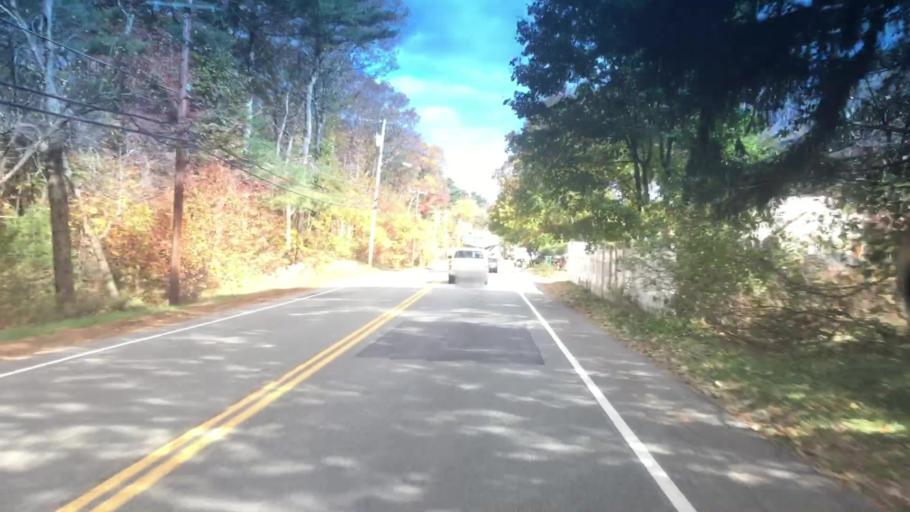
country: US
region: Massachusetts
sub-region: Norfolk County
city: Medfield
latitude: 42.1921
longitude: -71.2928
